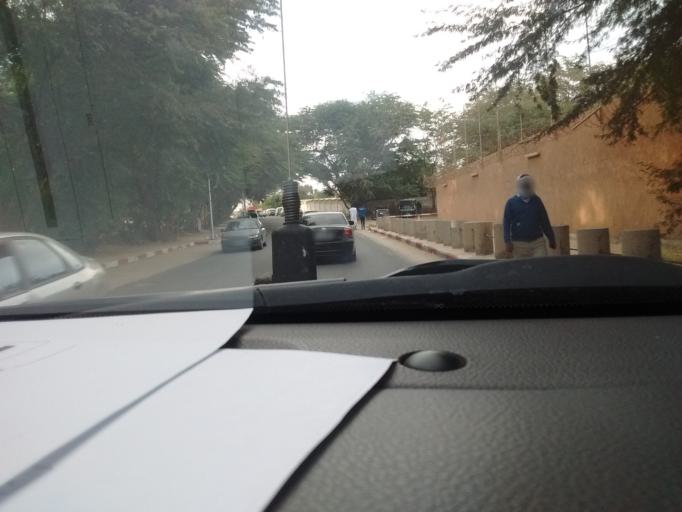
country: MR
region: Nouakchott
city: Nouakchott
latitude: 18.0920
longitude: -15.9835
